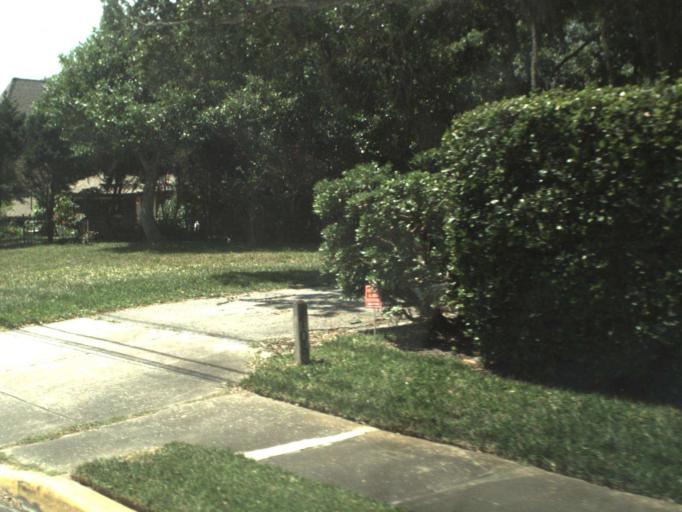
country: US
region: Florida
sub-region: Volusia County
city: Daytona Beach
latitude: 29.2067
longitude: -81.0033
